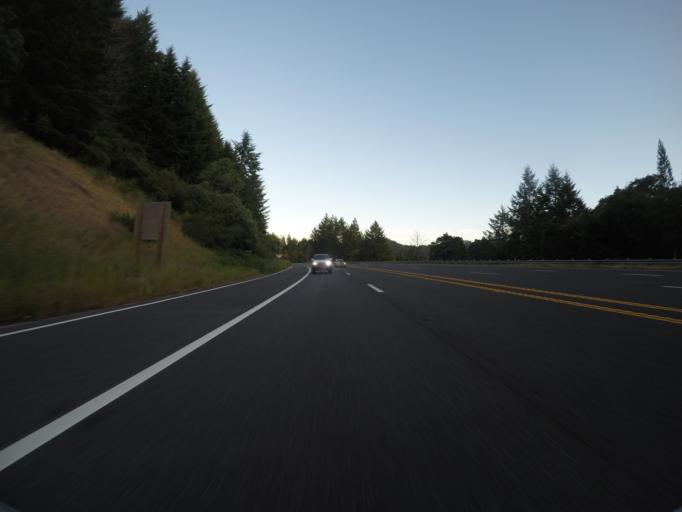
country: US
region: California
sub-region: Humboldt County
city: Redway
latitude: 39.9412
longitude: -123.7780
